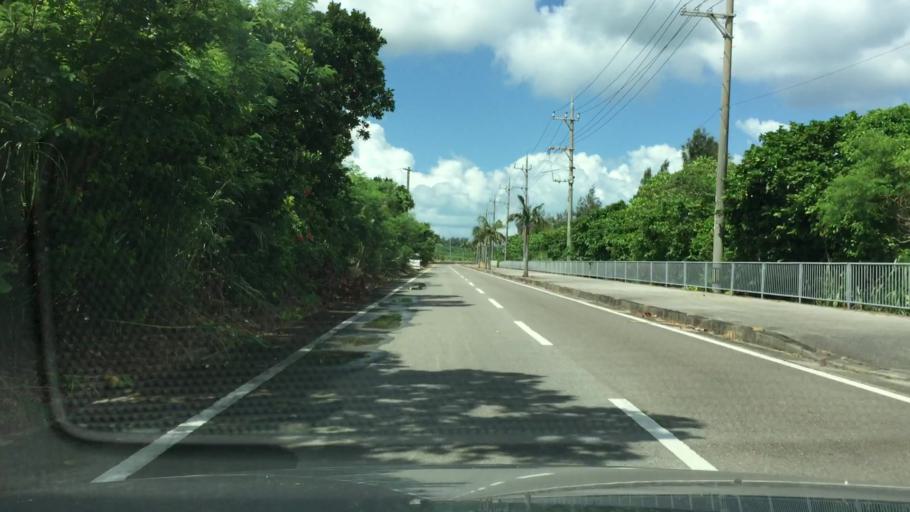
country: JP
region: Okinawa
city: Ishigaki
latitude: 24.3888
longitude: 124.1483
